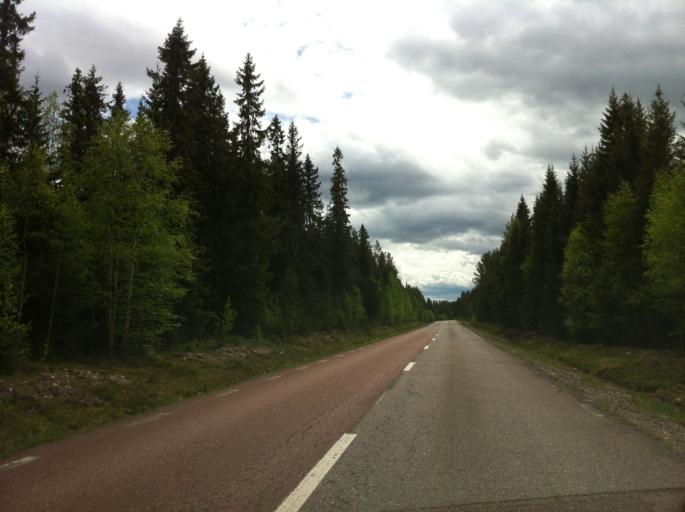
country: NO
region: Hedmark
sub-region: Trysil
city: Innbygda
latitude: 61.5255
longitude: 13.0800
